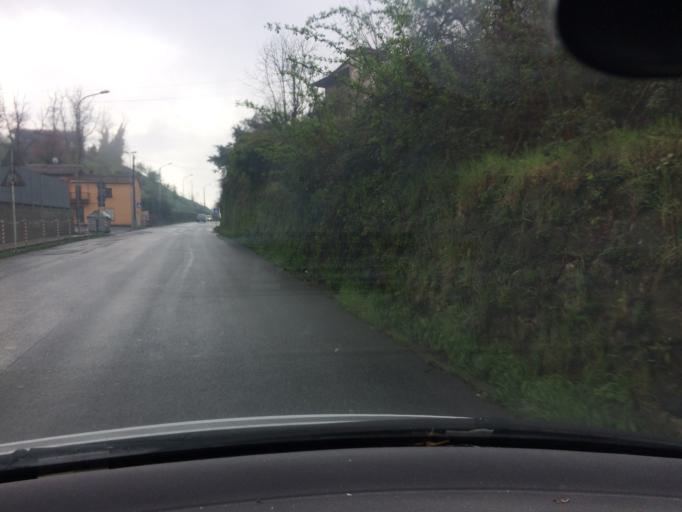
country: IT
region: Tuscany
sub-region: Provincia di Massa-Carrara
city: Massa
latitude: 44.0678
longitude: 10.1099
